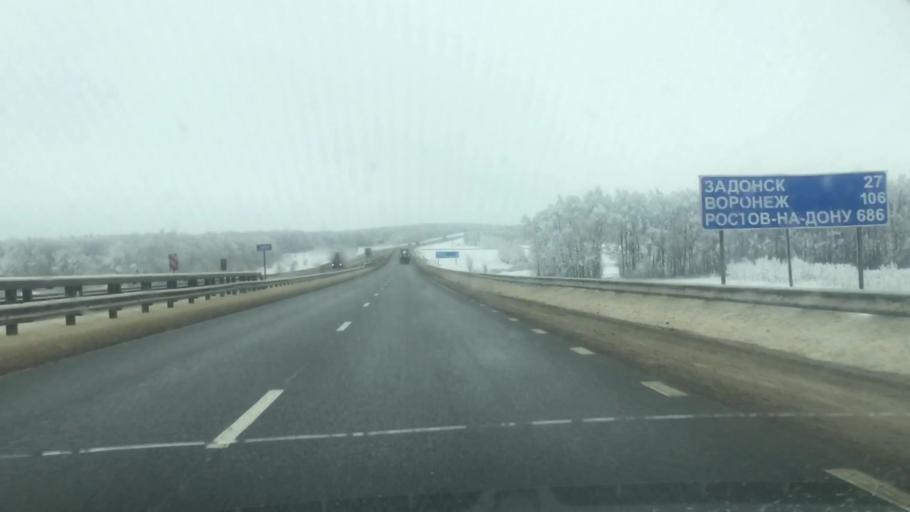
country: RU
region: Lipetsk
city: Yelets
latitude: 52.5402
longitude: 38.7265
